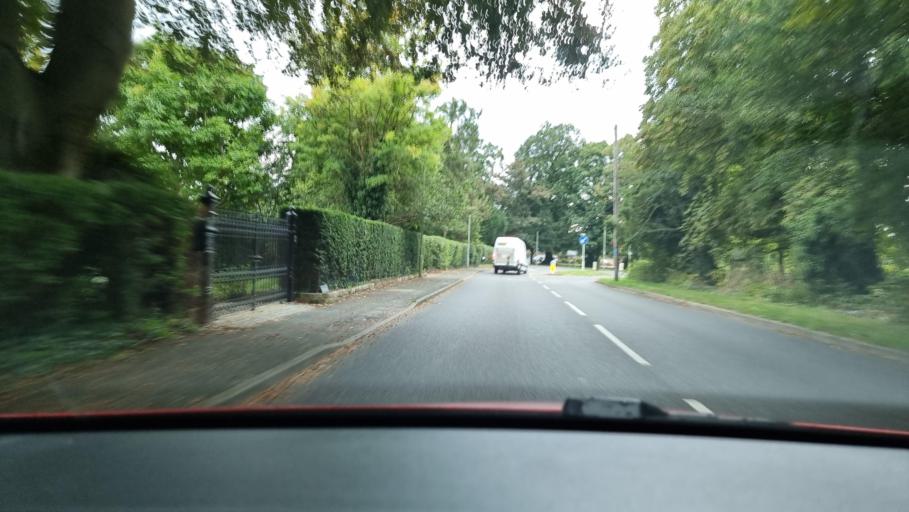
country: GB
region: England
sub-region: Hertfordshire
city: Tring
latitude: 51.7980
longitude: -0.6454
